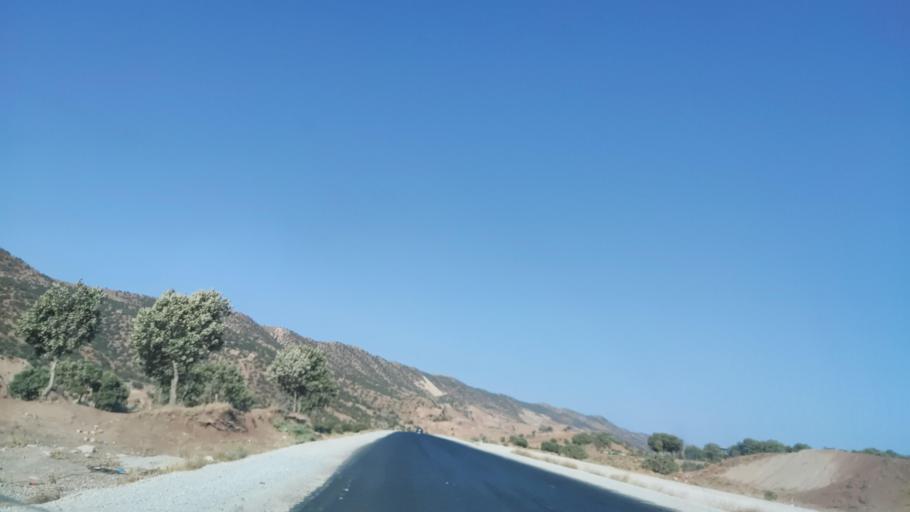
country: IQ
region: Arbil
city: Shaqlawah
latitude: 36.4300
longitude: 44.3281
